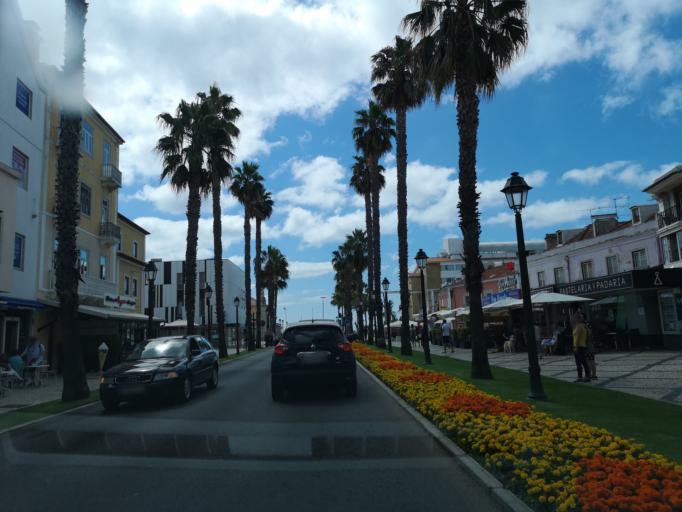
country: PT
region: Lisbon
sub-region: Cascais
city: Cascais
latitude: 38.6987
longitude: -9.4206
